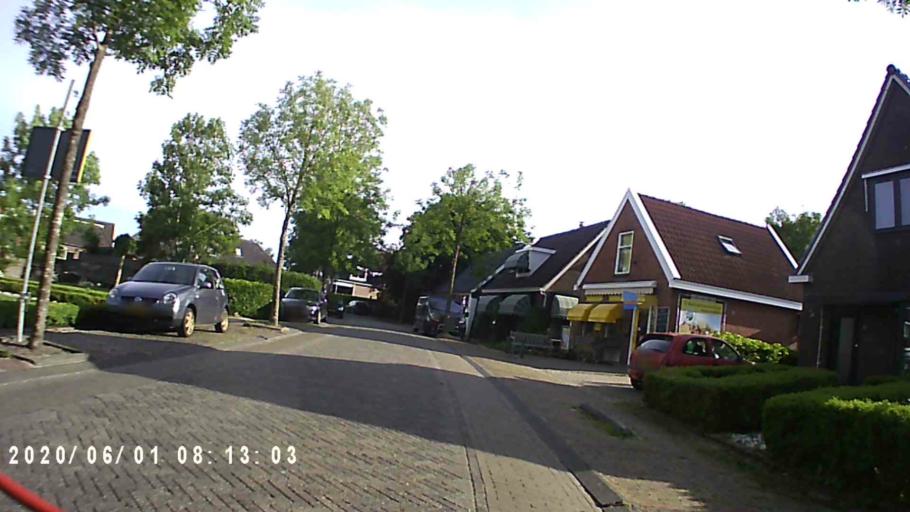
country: NL
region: Friesland
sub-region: Gemeente Ferwerderadiel
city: Burdaard
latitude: 53.2943
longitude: 5.8802
